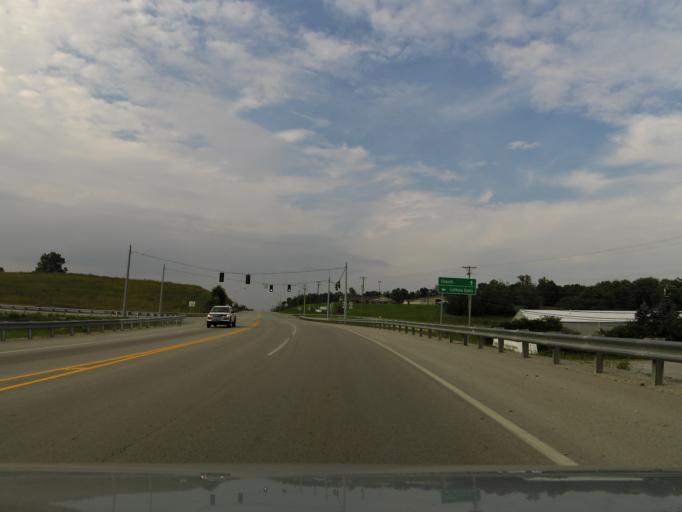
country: US
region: Kentucky
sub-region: Harrison County
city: Cynthiana
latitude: 38.3989
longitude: -84.2928
